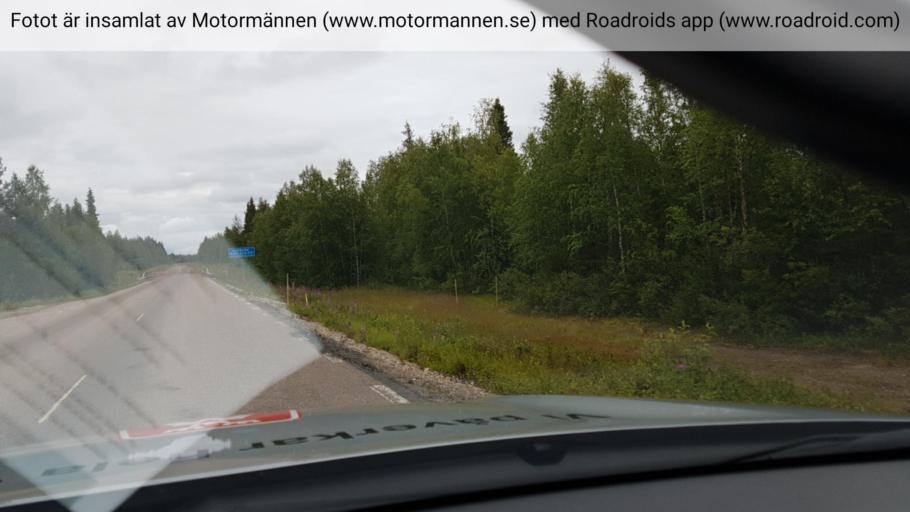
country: SE
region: Norrbotten
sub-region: Overkalix Kommun
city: OEverkalix
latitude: 67.0613
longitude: 22.3590
